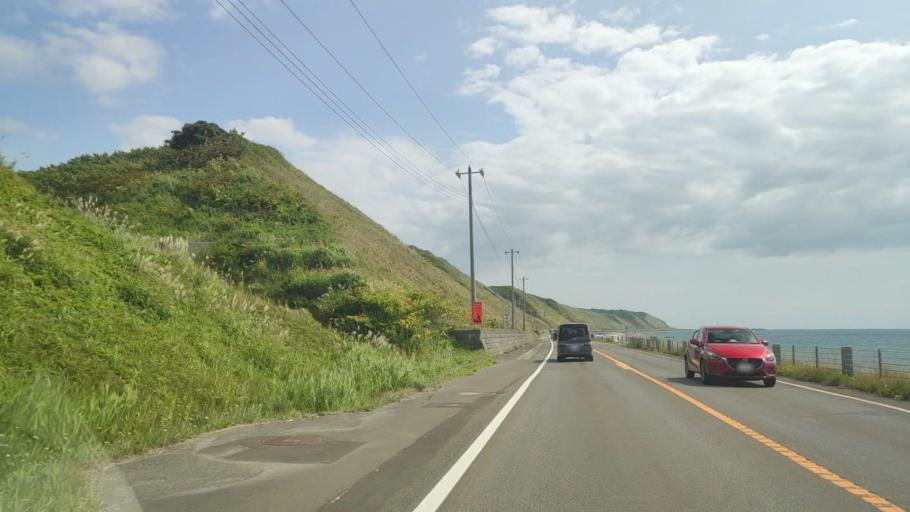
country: JP
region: Hokkaido
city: Rumoi
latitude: 44.2529
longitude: 141.6567
